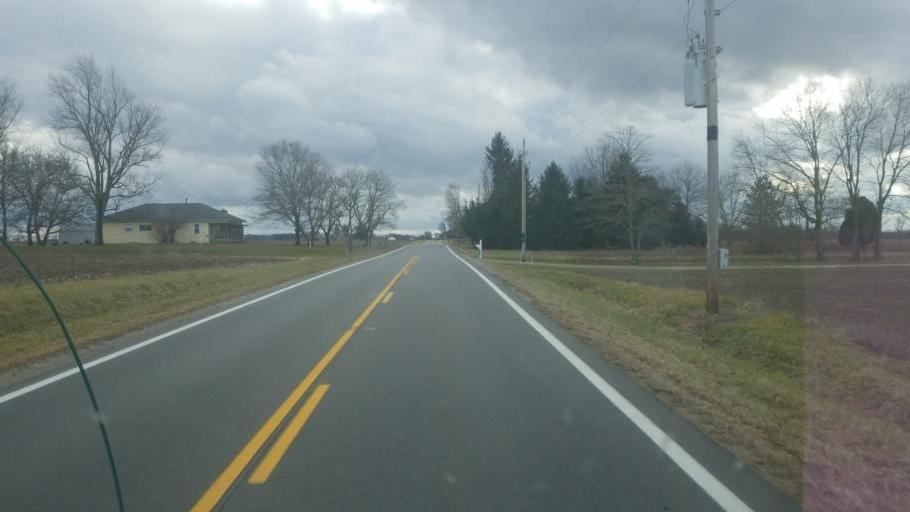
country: US
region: Ohio
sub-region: Crawford County
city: Bucyrus
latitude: 40.7682
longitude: -83.1308
